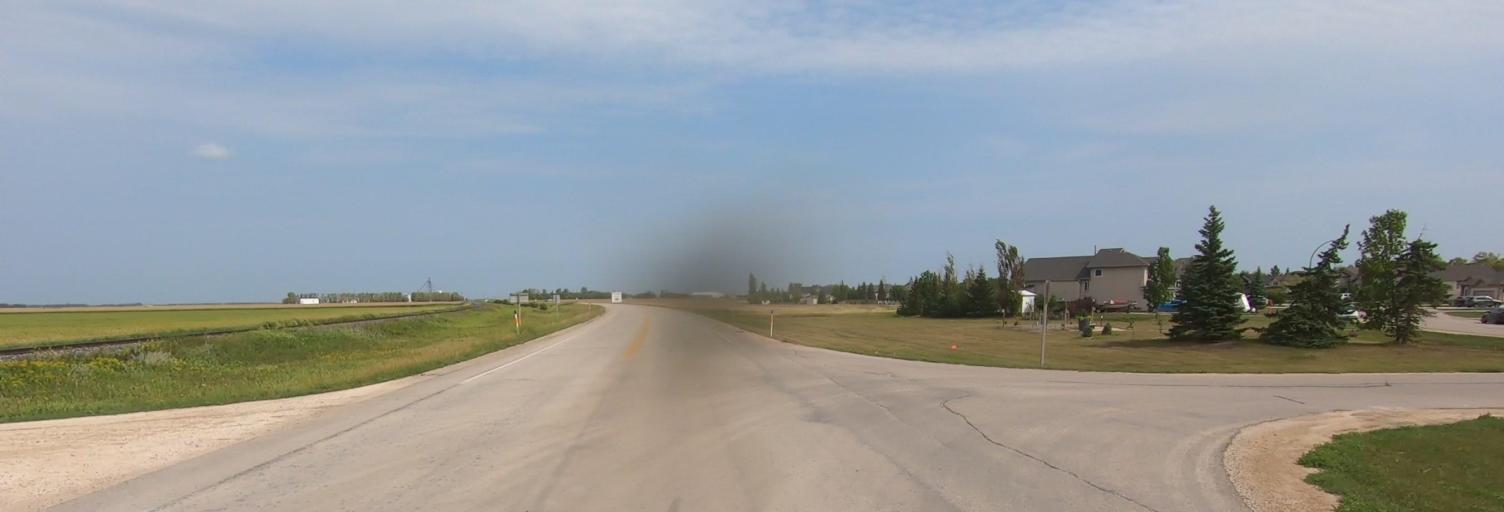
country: CA
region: Manitoba
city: Winnipeg
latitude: 49.6981
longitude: -97.2605
